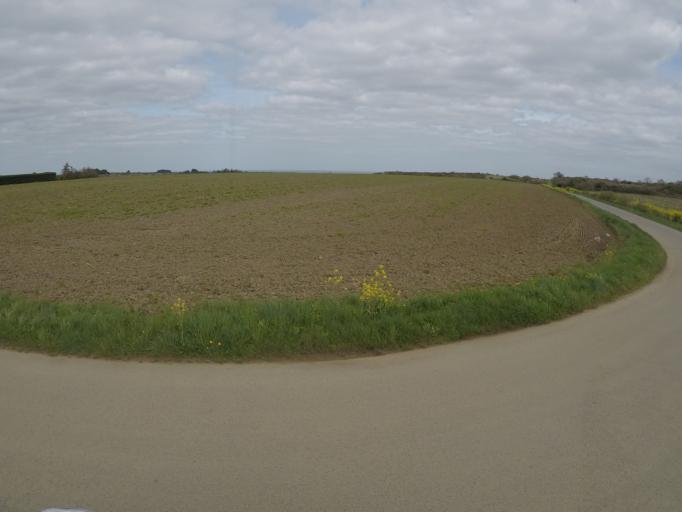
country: FR
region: Brittany
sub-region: Departement des Cotes-d'Armor
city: Plouezec
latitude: 48.7350
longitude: -2.9479
